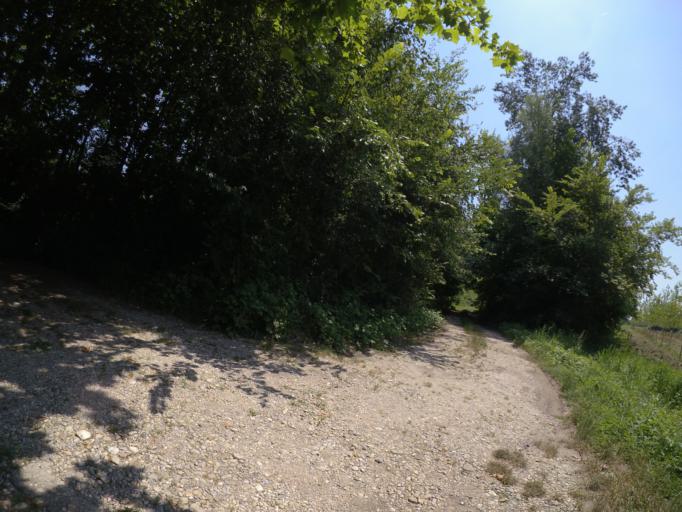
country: IT
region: Friuli Venezia Giulia
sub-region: Provincia di Udine
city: Rivignano
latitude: 45.9045
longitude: 13.0298
